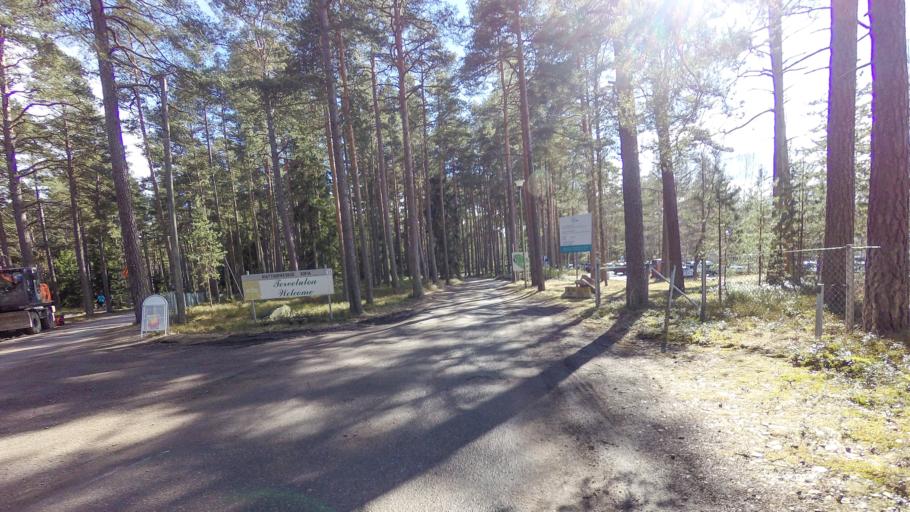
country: FI
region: Uusimaa
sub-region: Helsinki
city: Vantaa
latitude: 60.1916
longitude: 25.1377
